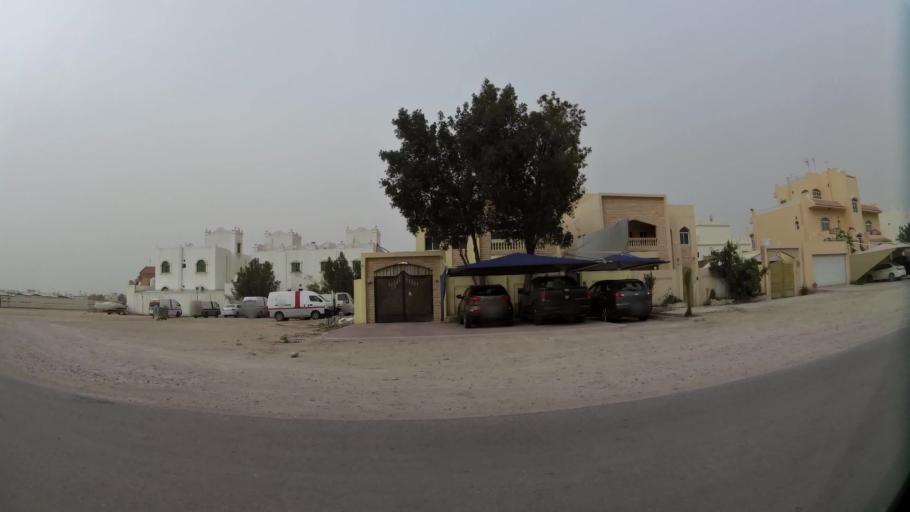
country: QA
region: Baladiyat ad Dawhah
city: Doha
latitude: 25.2515
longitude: 51.4949
